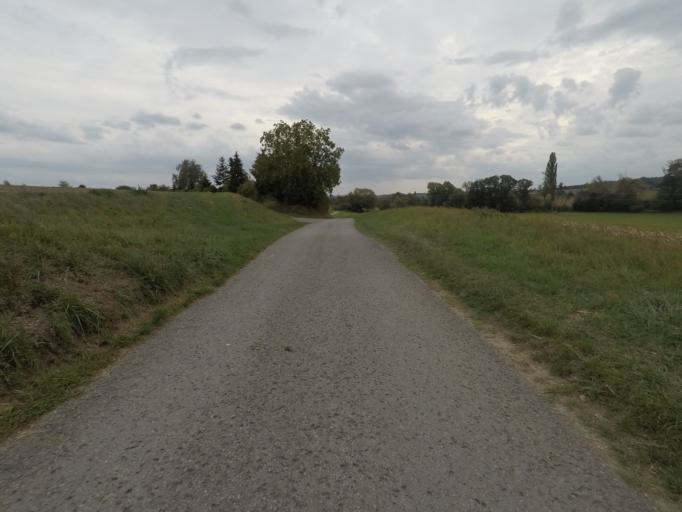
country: DE
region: Baden-Wuerttemberg
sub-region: Regierungsbezirk Stuttgart
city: Herrenberg
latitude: 48.5821
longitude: 8.8673
